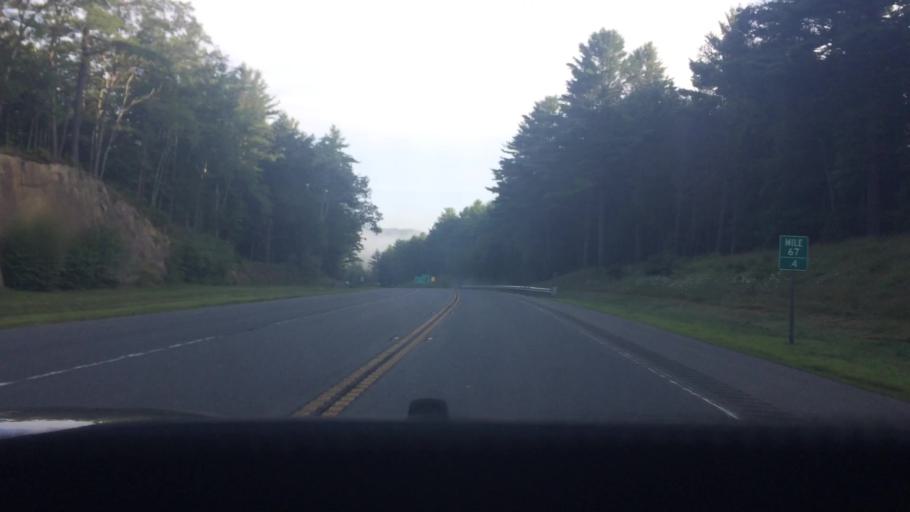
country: US
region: Massachusetts
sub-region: Franklin County
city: Orange
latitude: 42.5850
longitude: -72.3263
